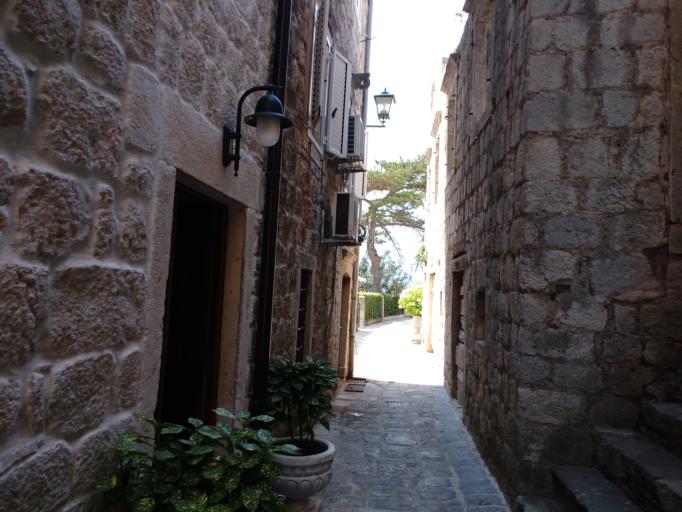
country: ME
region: Kotor
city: Risan
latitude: 42.4863
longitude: 18.6980
